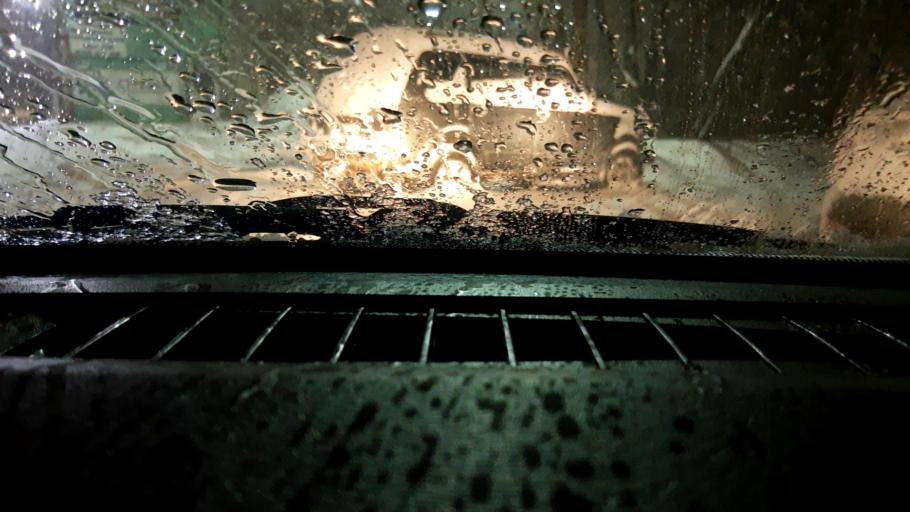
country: RU
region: Nizjnij Novgorod
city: Burevestnik
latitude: 56.2120
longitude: 43.8109
